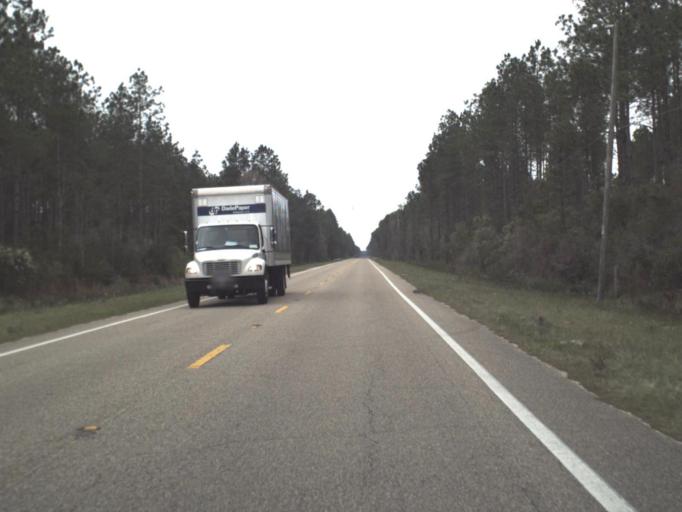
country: US
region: Florida
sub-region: Gulf County
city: Port Saint Joe
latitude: 29.8647
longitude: -85.2399
